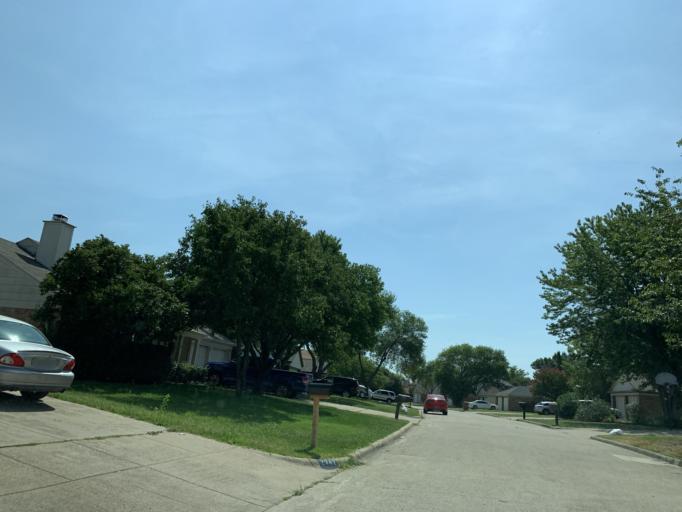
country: US
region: Texas
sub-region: Dallas County
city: Grand Prairie
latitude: 32.6676
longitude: -97.0355
